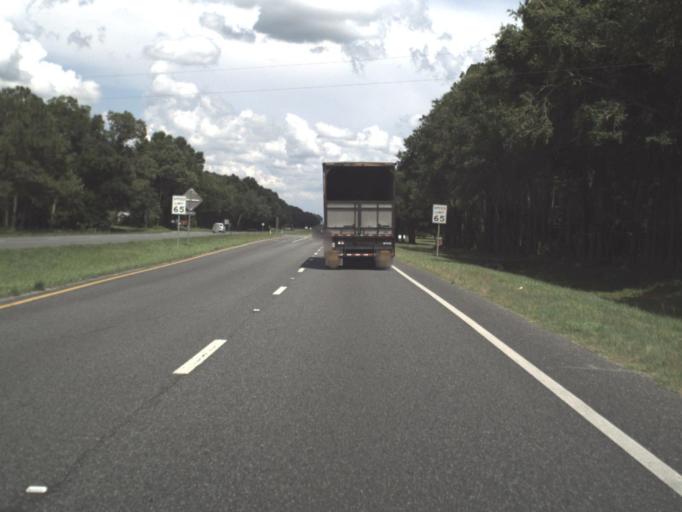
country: US
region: Florida
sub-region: Alachua County
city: High Springs
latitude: 29.8109
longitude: -82.5595
